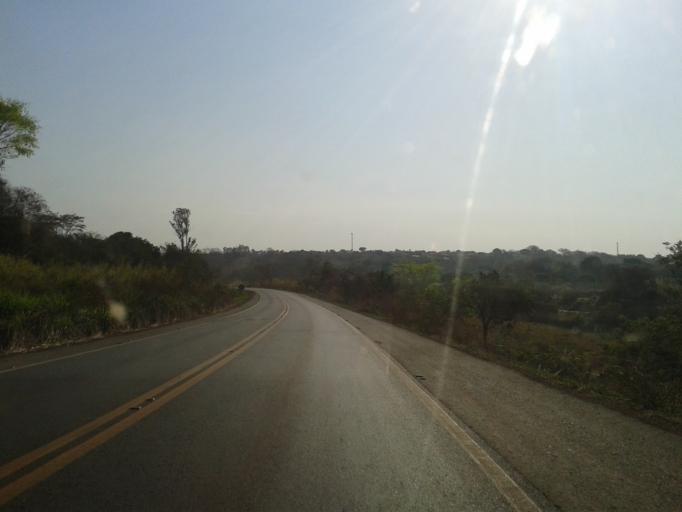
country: BR
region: Minas Gerais
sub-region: Ituiutaba
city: Ituiutaba
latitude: -18.9618
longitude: -49.4735
